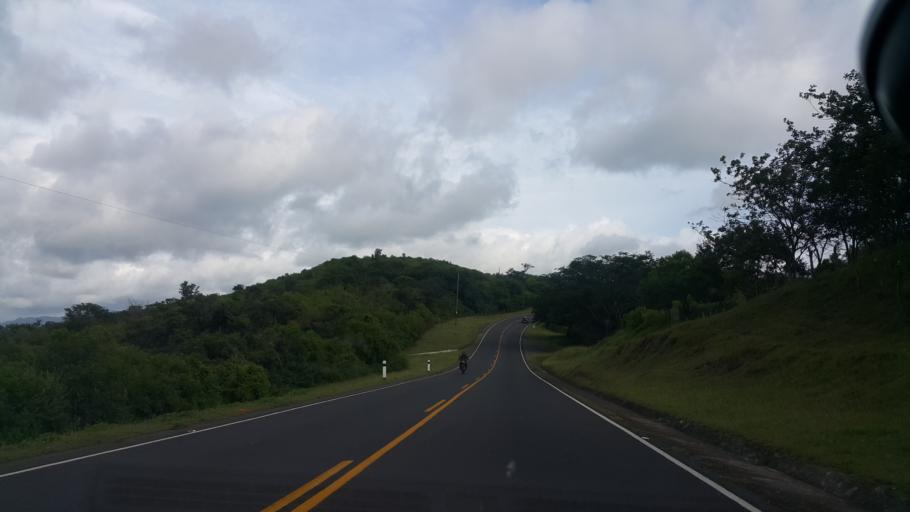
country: NI
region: Matagalpa
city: Matagalpa
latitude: 12.9518
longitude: -86.0235
